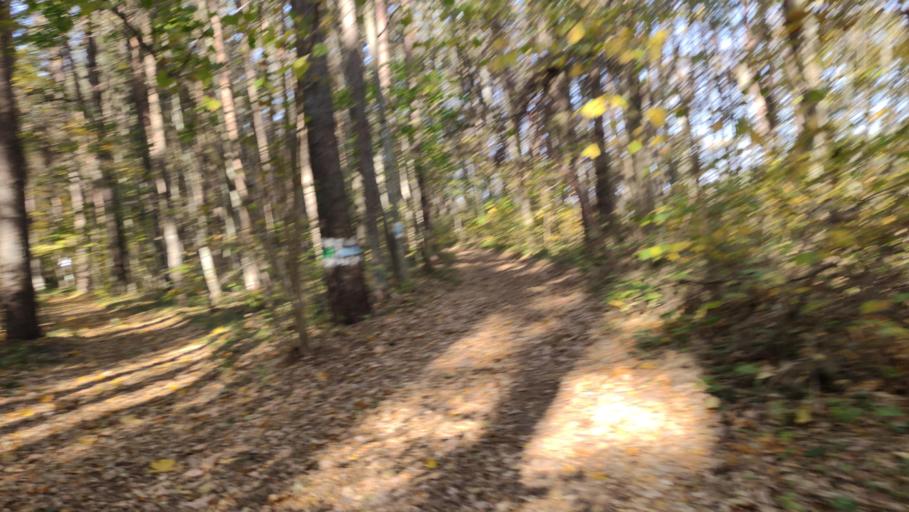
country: LT
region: Alytaus apskritis
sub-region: Alytus
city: Alytus
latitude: 54.3725
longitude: 24.0915
